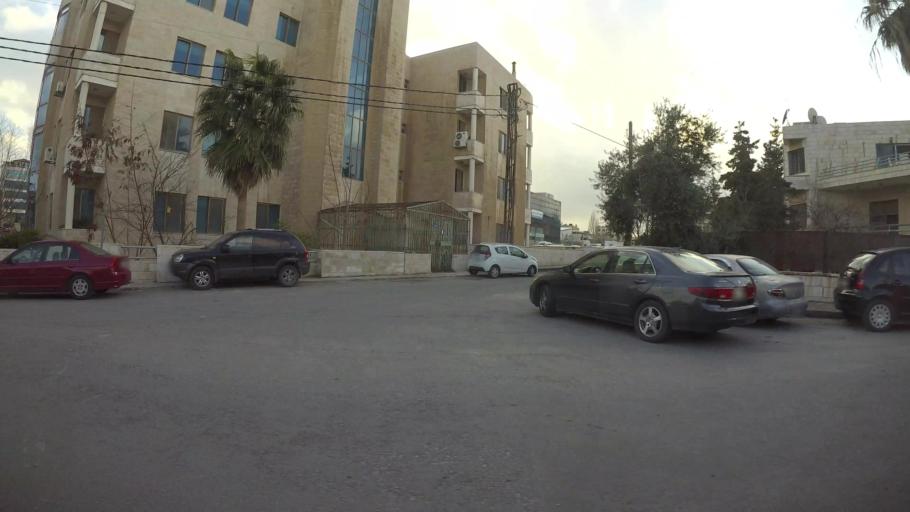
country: JO
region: Amman
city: Wadi as Sir
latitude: 31.9777
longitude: 35.8544
